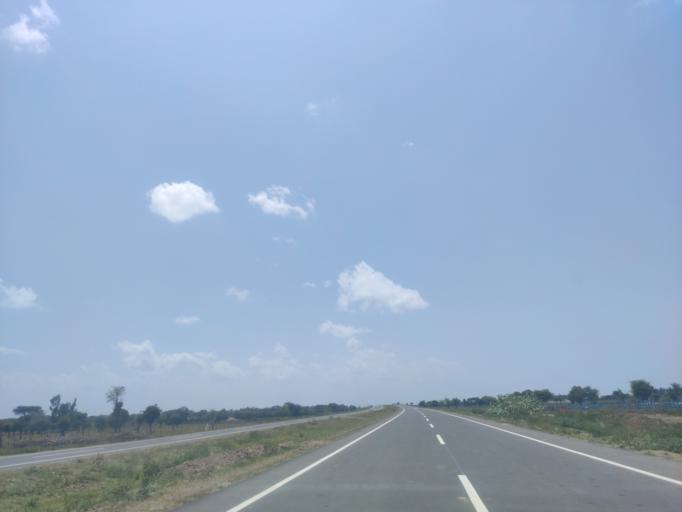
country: ET
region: Oromiya
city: Mojo
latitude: 8.3477
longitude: 38.9795
